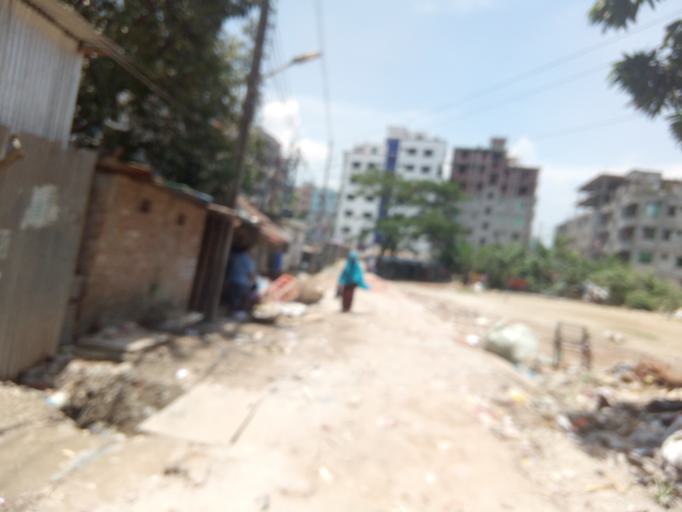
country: BD
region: Dhaka
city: Paltan
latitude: 23.7568
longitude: 90.4411
